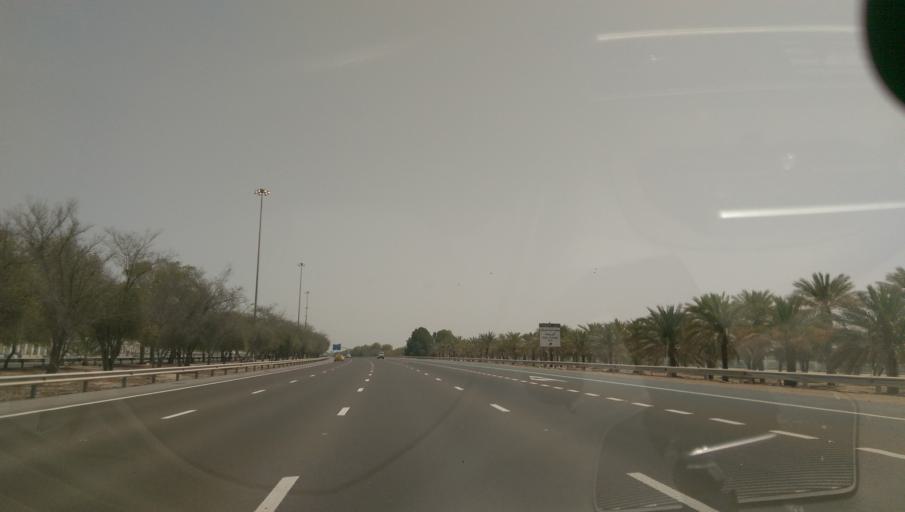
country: AE
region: Abu Dhabi
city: Abu Dhabi
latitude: 24.5224
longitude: 54.6912
